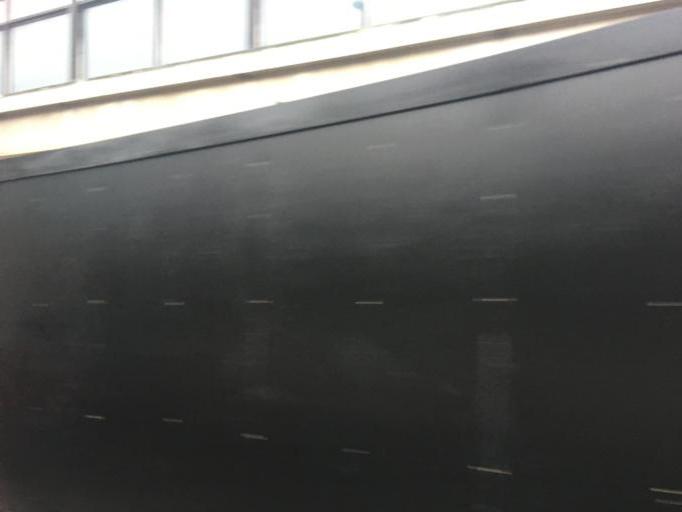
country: GB
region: England
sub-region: Coventry
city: Coventry
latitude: 52.4069
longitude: -1.5072
